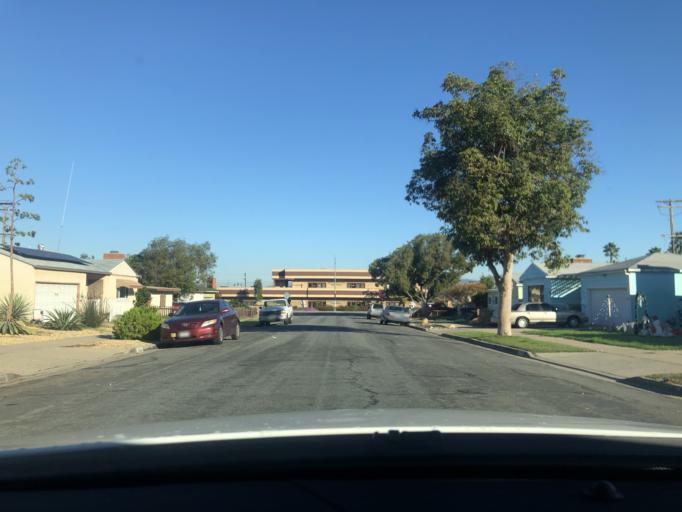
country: US
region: California
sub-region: San Diego County
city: El Cajon
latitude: 32.7791
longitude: -116.9591
